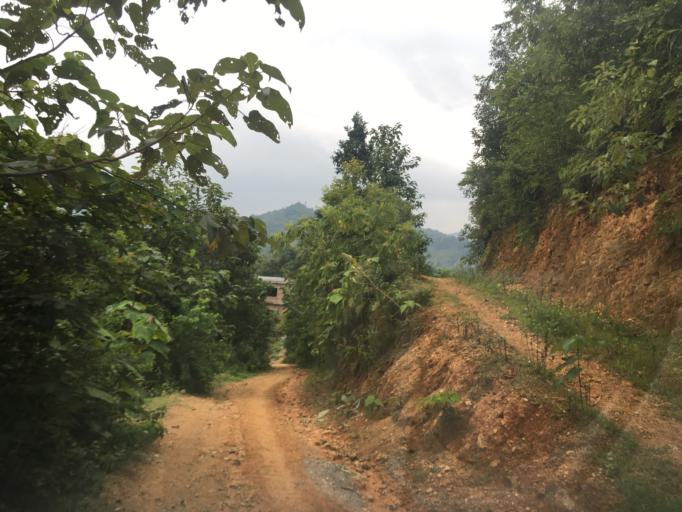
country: CN
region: Guangxi Zhuangzu Zizhiqu
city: Xinzhou
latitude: 25.1644
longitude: 105.6981
